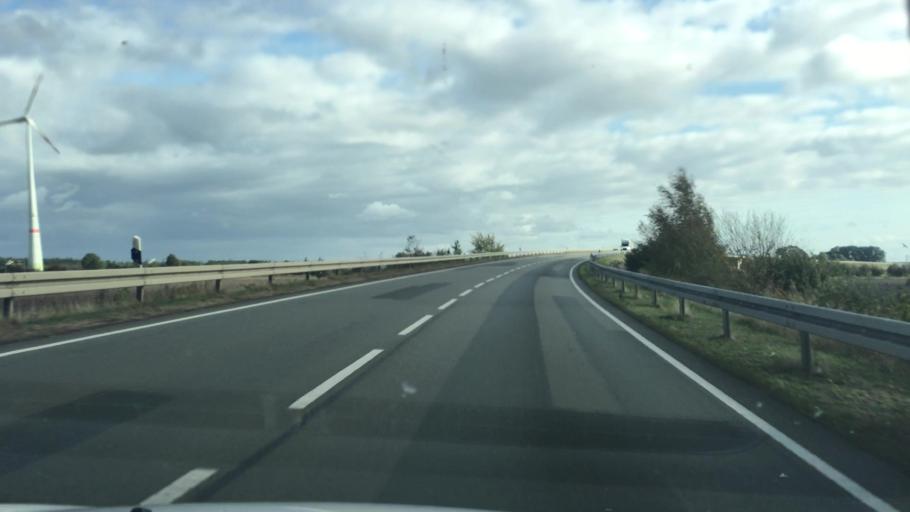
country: DE
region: Lower Saxony
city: Diepholz
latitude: 52.6266
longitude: 8.4061
